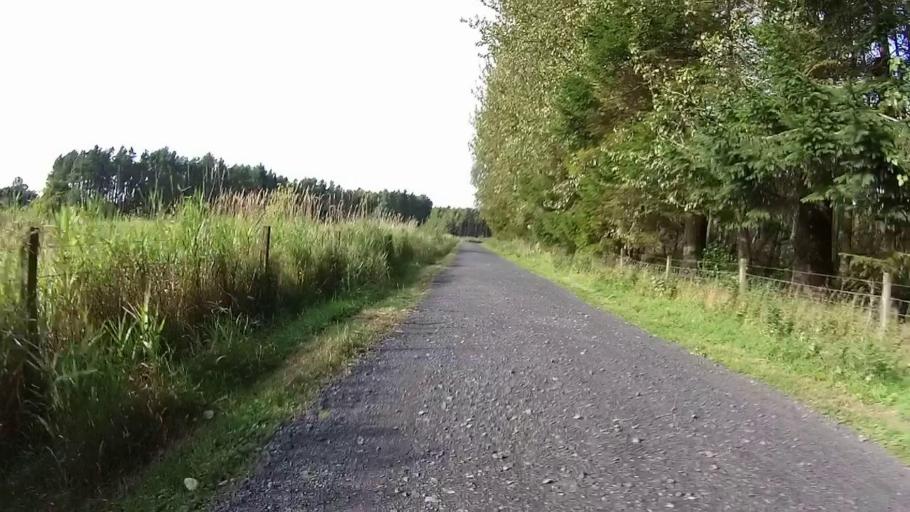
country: GB
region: Scotland
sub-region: Perth and Kinross
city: Kinross
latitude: 56.2050
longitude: -3.4068
